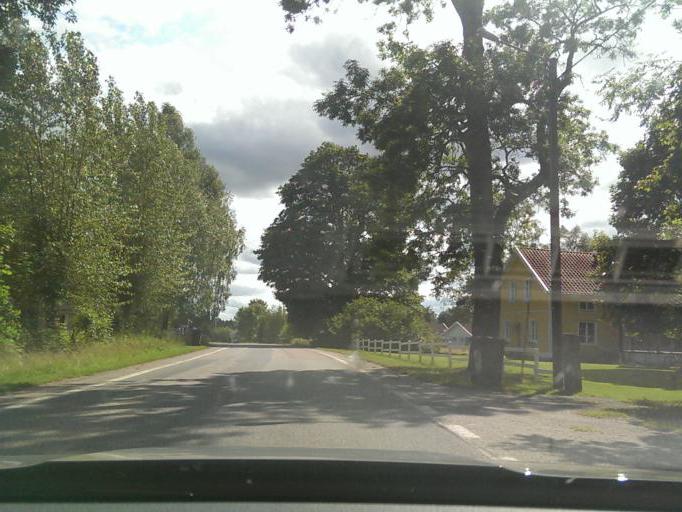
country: SE
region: Joenkoeping
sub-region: Varnamo Kommun
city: Forsheda
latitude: 57.0673
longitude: 13.8611
